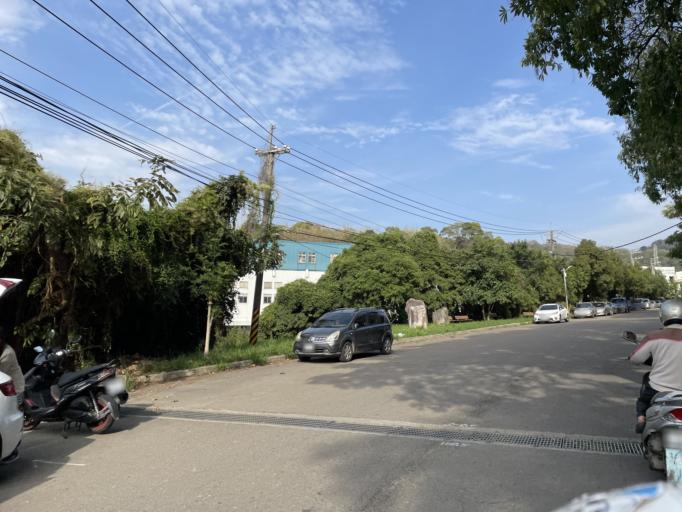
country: TW
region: Taiwan
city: Fengyuan
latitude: 24.2179
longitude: 120.7263
